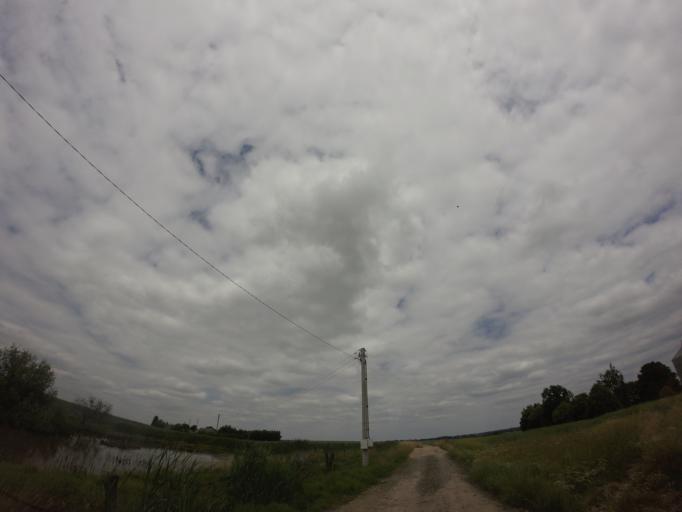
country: PL
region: West Pomeranian Voivodeship
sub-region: Powiat choszczenski
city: Krzecin
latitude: 53.0744
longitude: 15.5237
